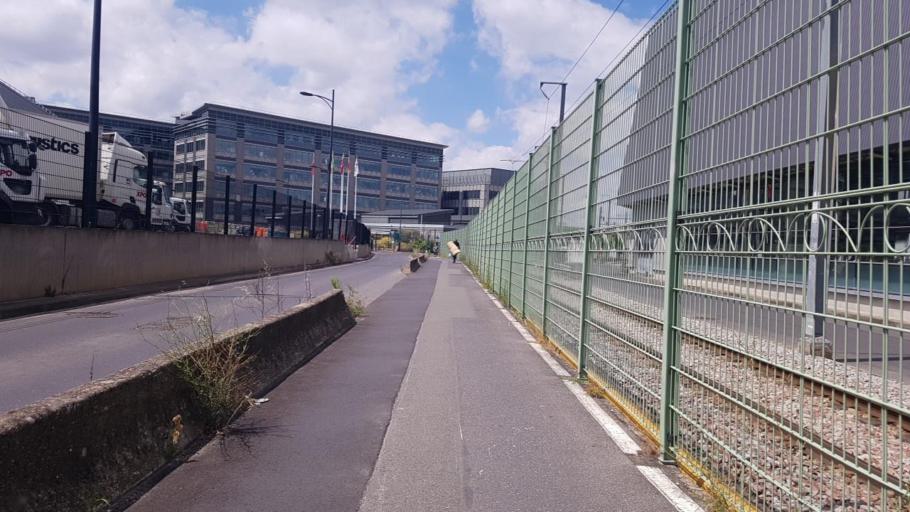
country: FR
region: Ile-de-France
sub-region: Departement de Seine-Saint-Denis
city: Pantin
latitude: 48.8965
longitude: 2.4166
